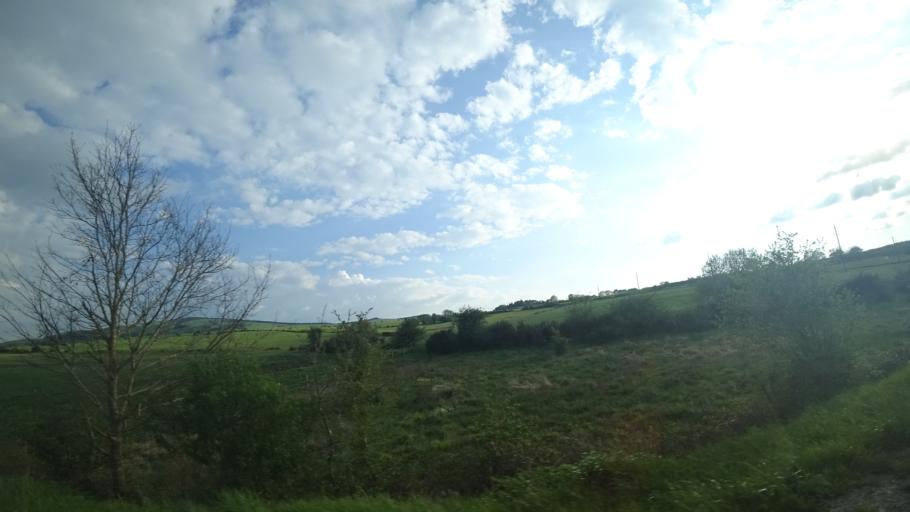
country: FR
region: Midi-Pyrenees
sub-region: Departement de l'Aveyron
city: Severac-le-Chateau
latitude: 44.2489
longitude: 2.9310
